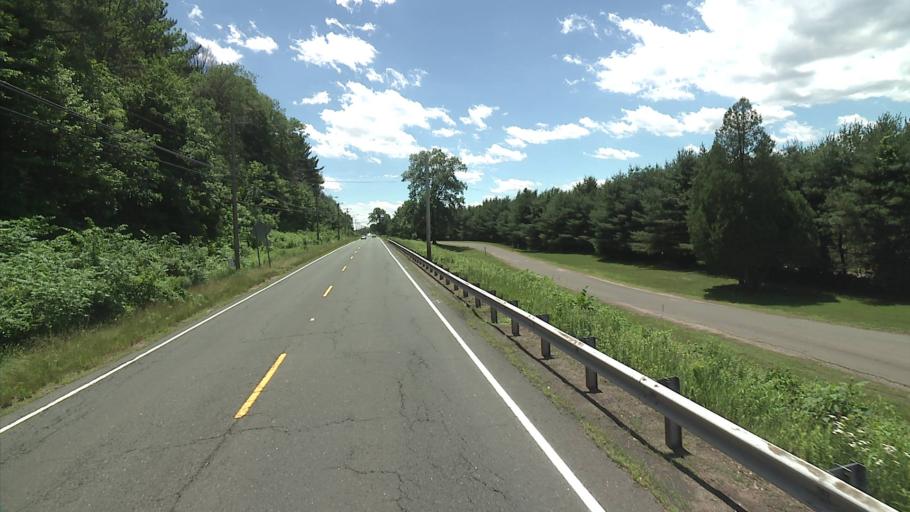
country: US
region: Massachusetts
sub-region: Hampden County
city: East Longmeadow
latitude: 42.0204
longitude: -72.5145
